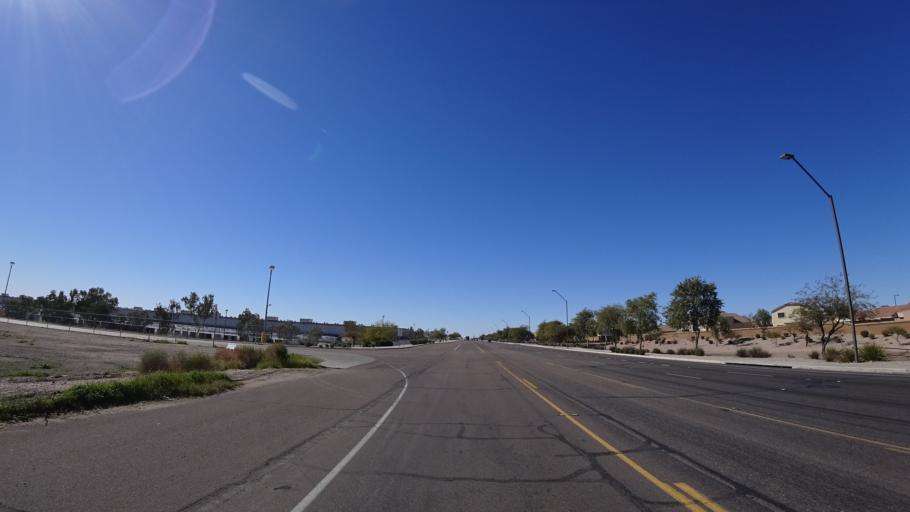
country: US
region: Arizona
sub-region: Maricopa County
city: Buckeye
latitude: 33.3920
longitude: -112.5591
